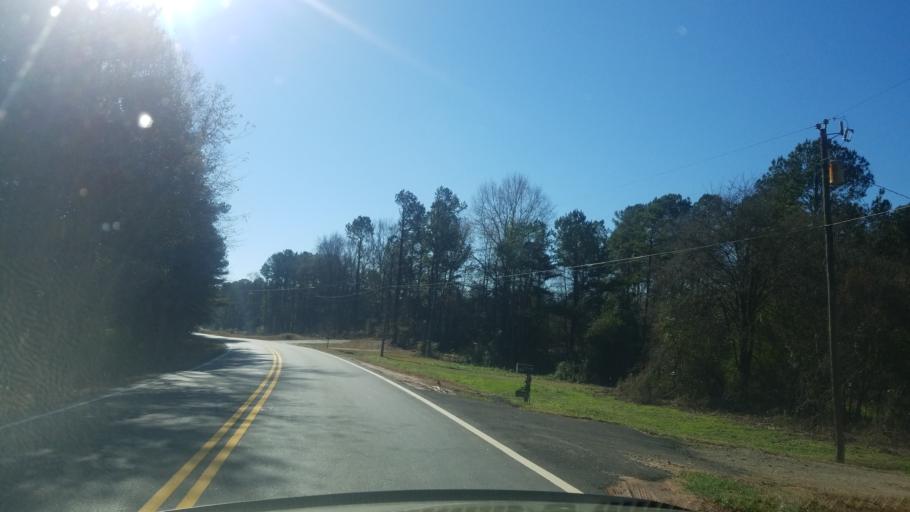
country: US
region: Alabama
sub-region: Chambers County
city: Valley
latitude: 32.8205
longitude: -85.1069
